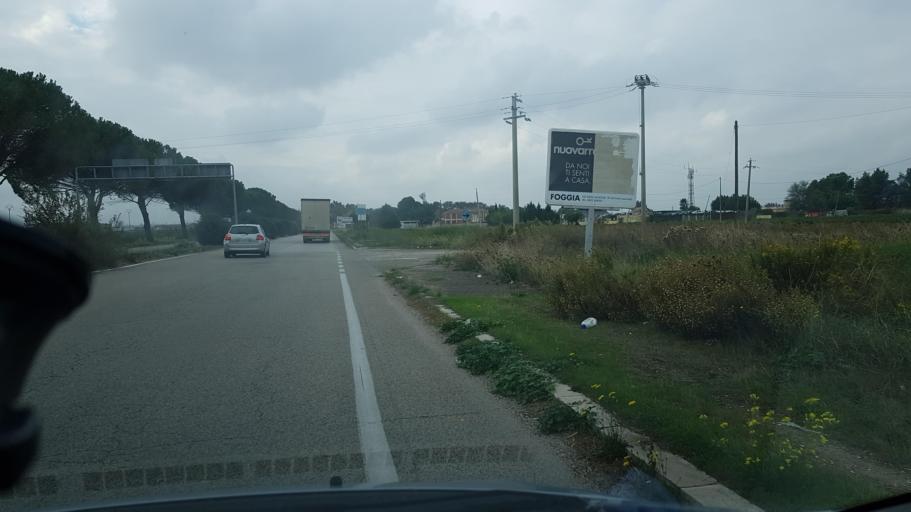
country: IT
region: Apulia
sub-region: Provincia di Foggia
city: Foggia
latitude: 41.4889
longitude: 15.5657
